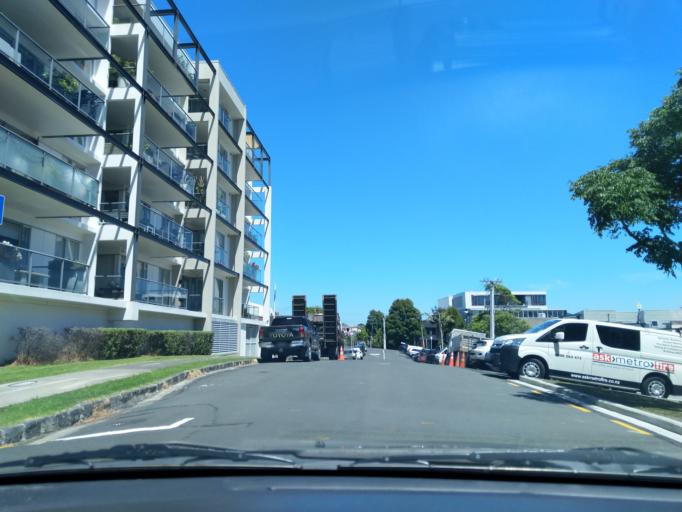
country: NZ
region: Auckland
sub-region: Auckland
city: Auckland
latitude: -36.8710
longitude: 174.7461
